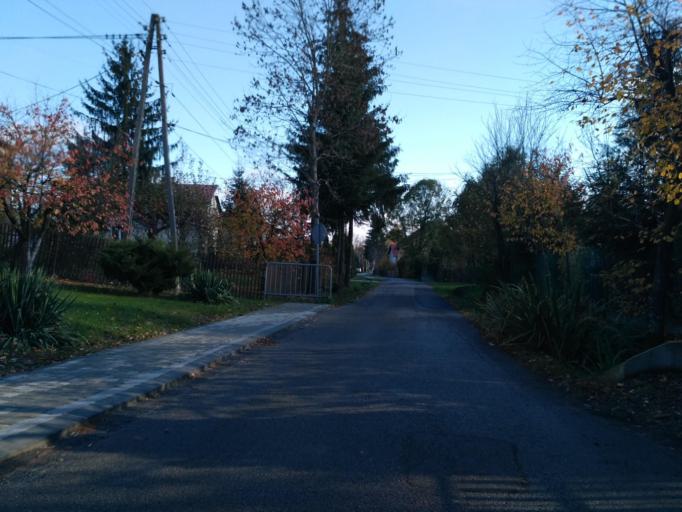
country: PL
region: Subcarpathian Voivodeship
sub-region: Powiat rzeszowski
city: Niechobrz
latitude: 49.9962
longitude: 21.8781
